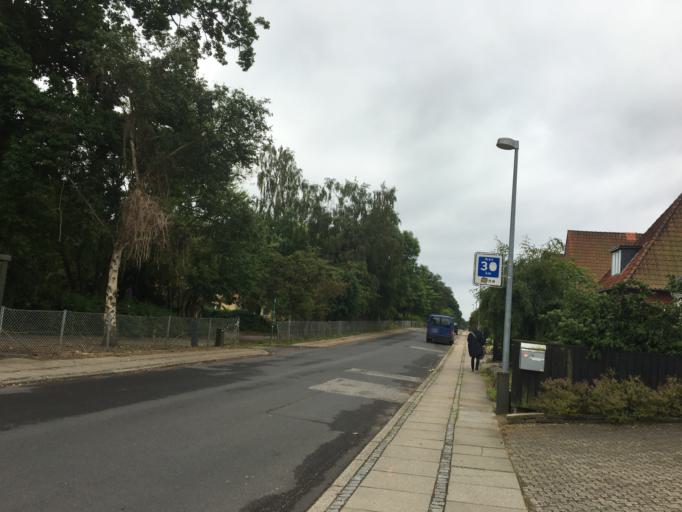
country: DK
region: South Denmark
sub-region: Middelfart Kommune
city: Middelfart
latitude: 55.5012
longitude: 9.7227
